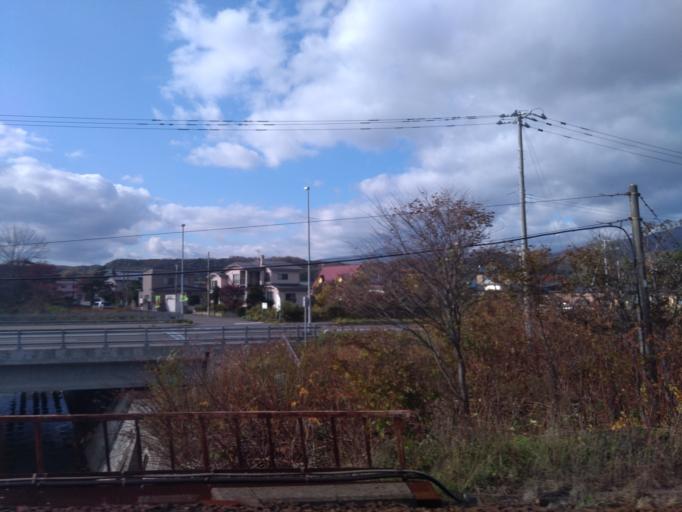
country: JP
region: Hokkaido
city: Shiraoi
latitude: 42.4484
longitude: 141.1746
